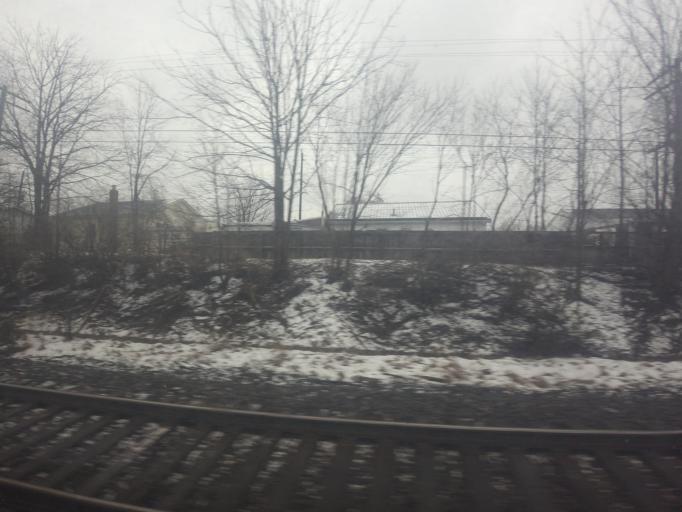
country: CA
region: Ontario
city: Belleville
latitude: 44.1735
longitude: -77.3905
